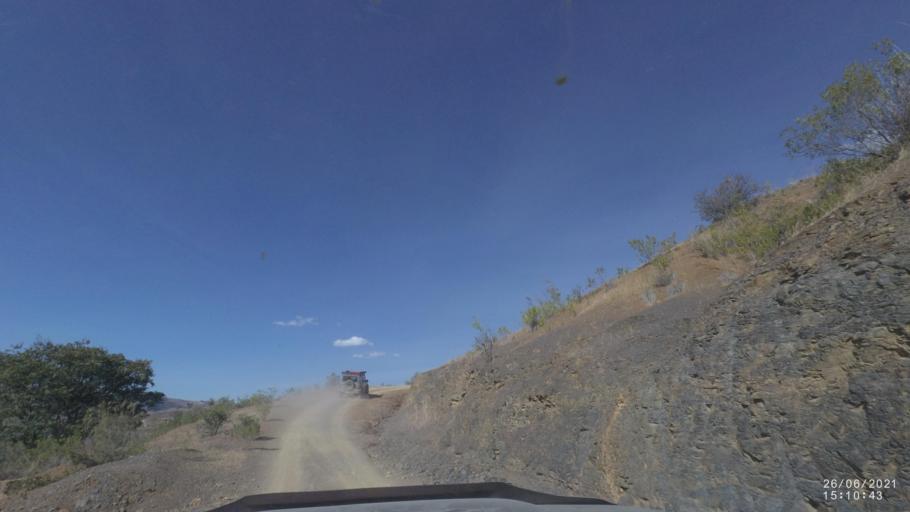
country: BO
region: Cochabamba
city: Mizque
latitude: -17.9540
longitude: -65.6421
